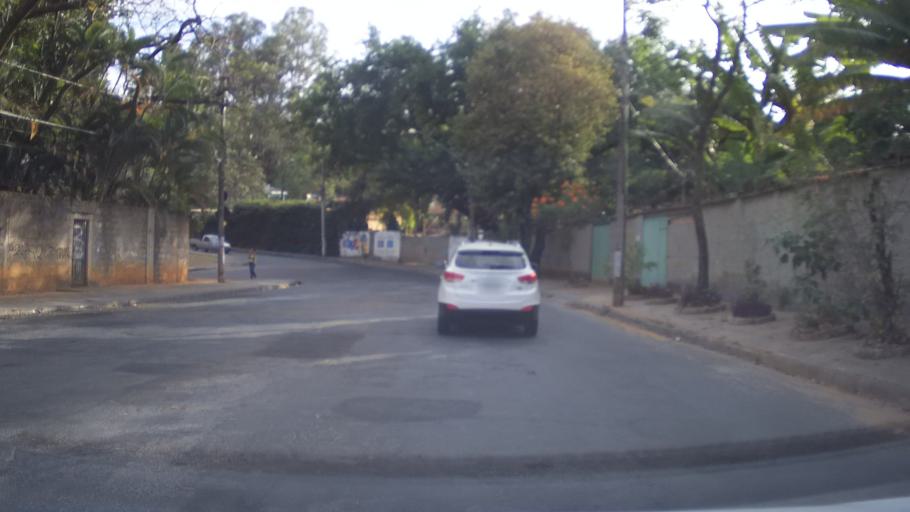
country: BR
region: Minas Gerais
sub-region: Belo Horizonte
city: Belo Horizonte
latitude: -19.8675
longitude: -43.9962
